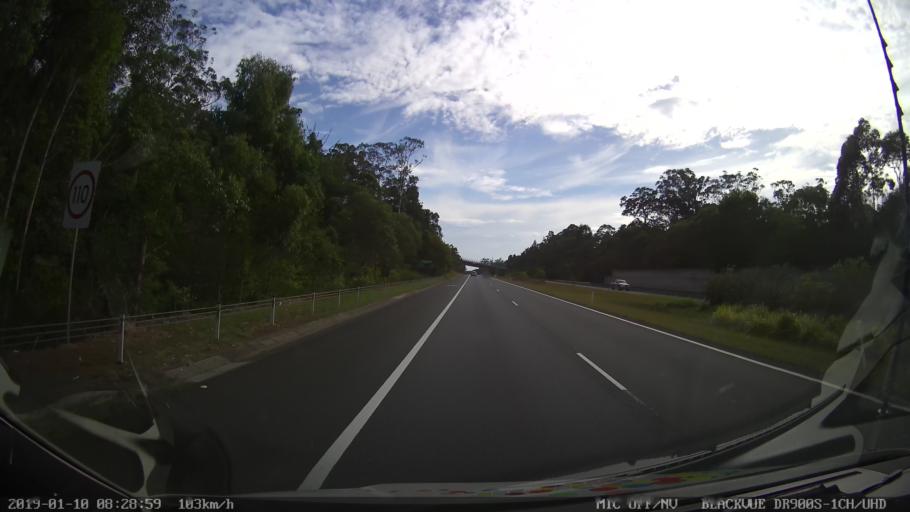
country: AU
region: New South Wales
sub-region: Coffs Harbour
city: Bonville
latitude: -30.3874
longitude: 153.0396
